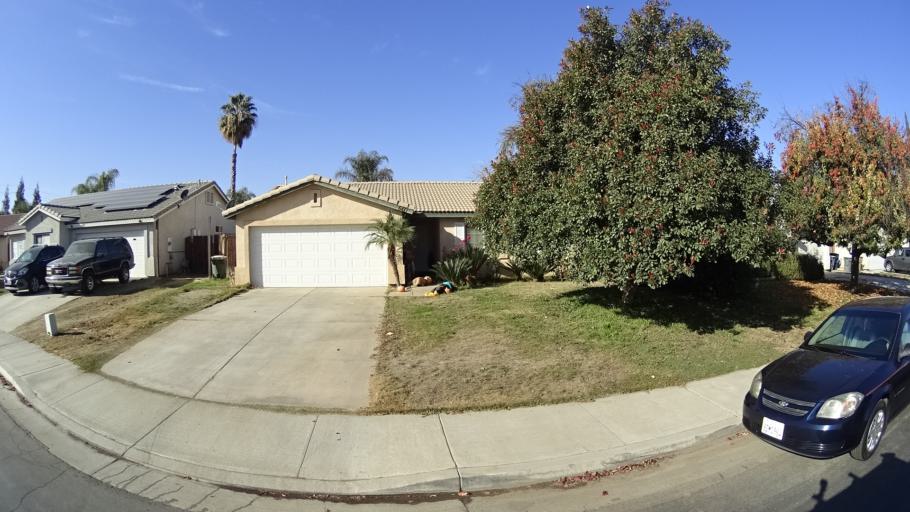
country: US
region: California
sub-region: Kern County
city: Greenfield
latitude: 35.2971
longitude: -119.0666
